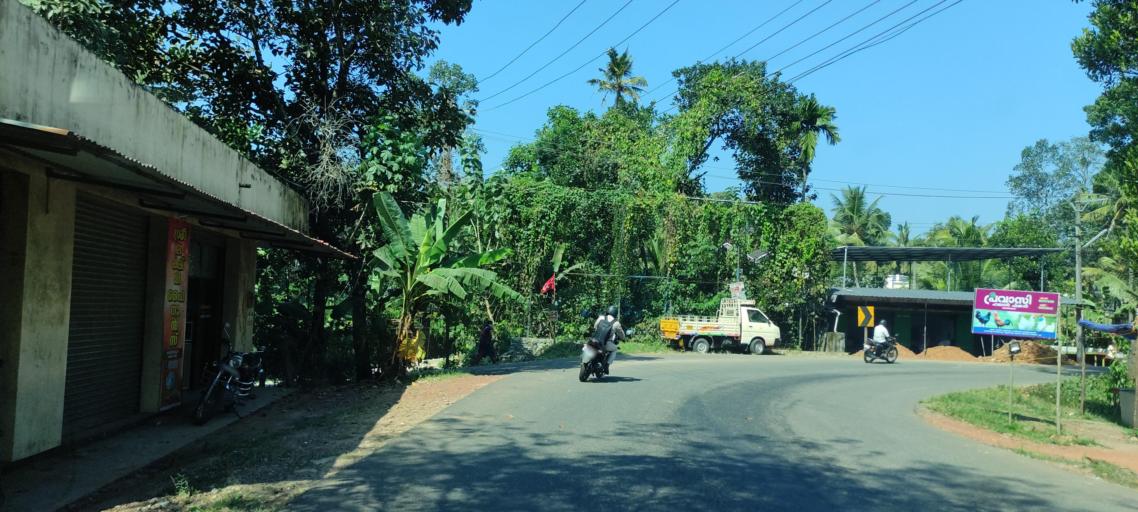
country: IN
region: Kerala
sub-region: Kollam
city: Panmana
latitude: 9.0448
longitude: 76.5764
